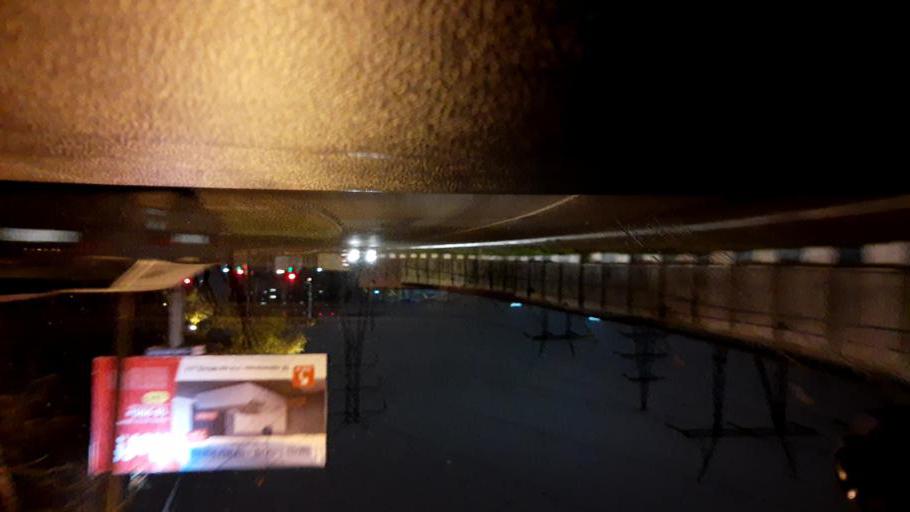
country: RU
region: Moskovskaya
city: Reutov
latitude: 55.7614
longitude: 37.8469
